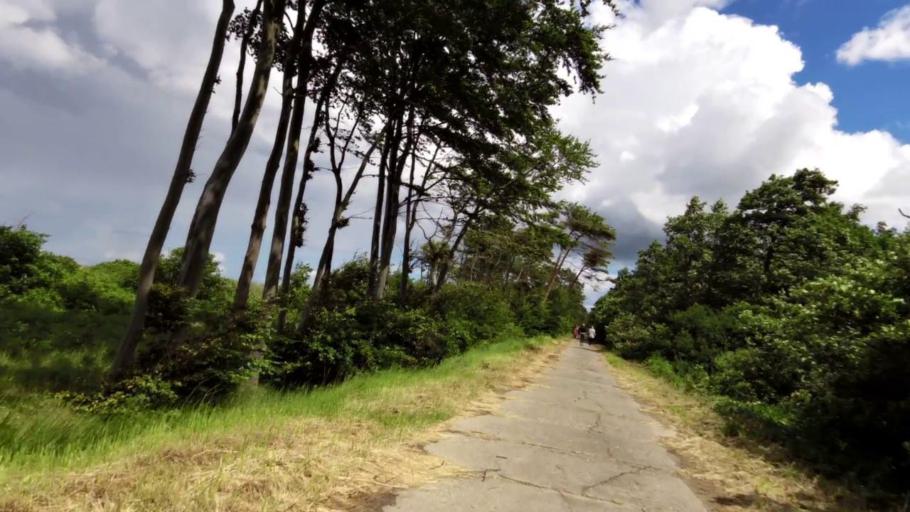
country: PL
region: West Pomeranian Voivodeship
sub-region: Powiat slawienski
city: Darlowo
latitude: 54.4947
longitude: 16.4455
